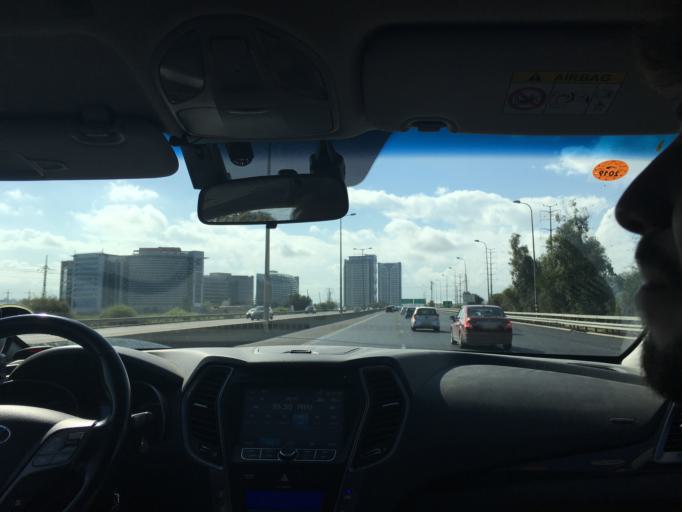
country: IL
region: Tel Aviv
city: Giv`at Shemu'el
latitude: 32.1065
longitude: 34.8489
